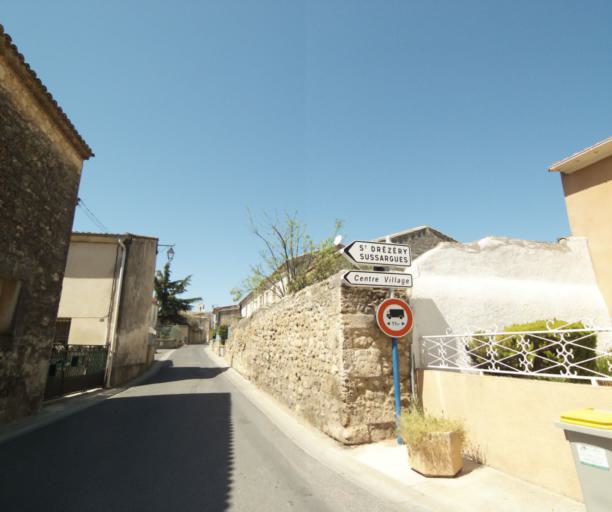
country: FR
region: Languedoc-Roussillon
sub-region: Departement de l'Herault
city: Beaulieu
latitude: 43.7281
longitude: 4.0228
